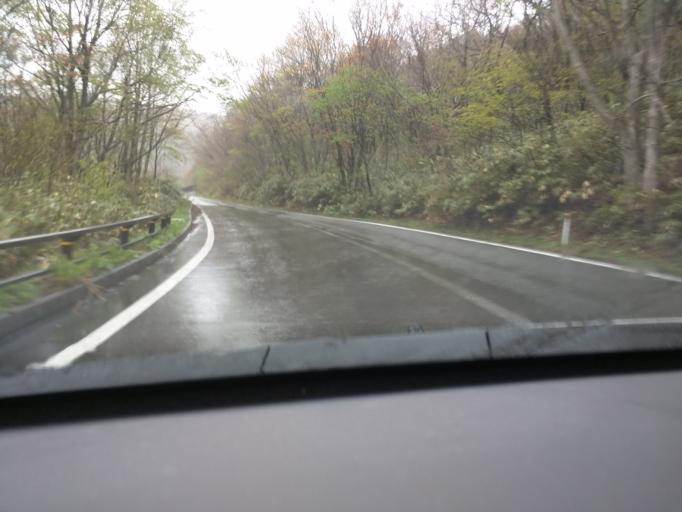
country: JP
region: Fukushima
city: Inawashiro
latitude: 37.6597
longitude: 140.2591
